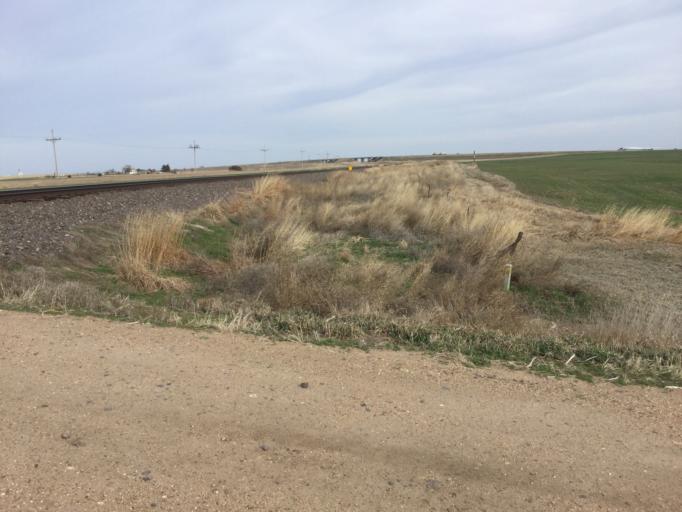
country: US
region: Kansas
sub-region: Ellis County
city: Ellis
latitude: 38.9724
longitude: -99.7035
